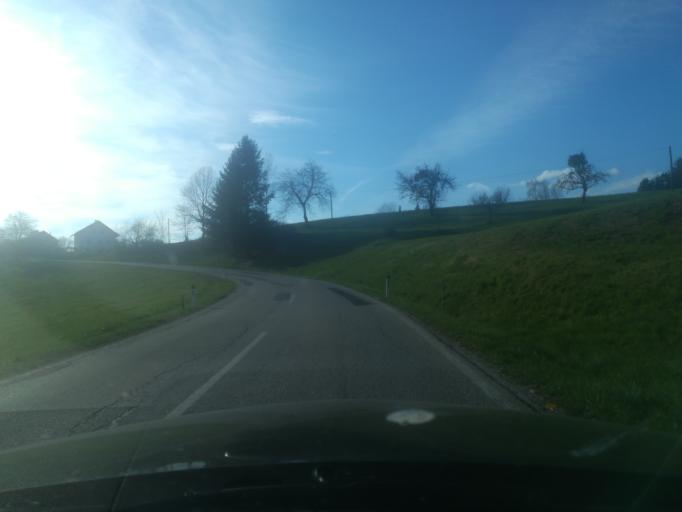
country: AT
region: Upper Austria
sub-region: Politischer Bezirk Perg
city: Bad Kreuzen
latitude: 48.2634
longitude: 14.7991
